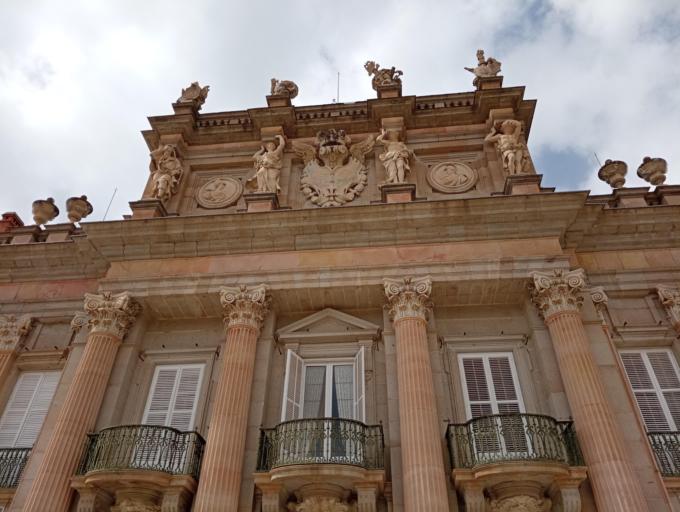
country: ES
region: Castille and Leon
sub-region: Provincia de Segovia
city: San Ildefonso
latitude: 40.8975
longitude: -4.0042
